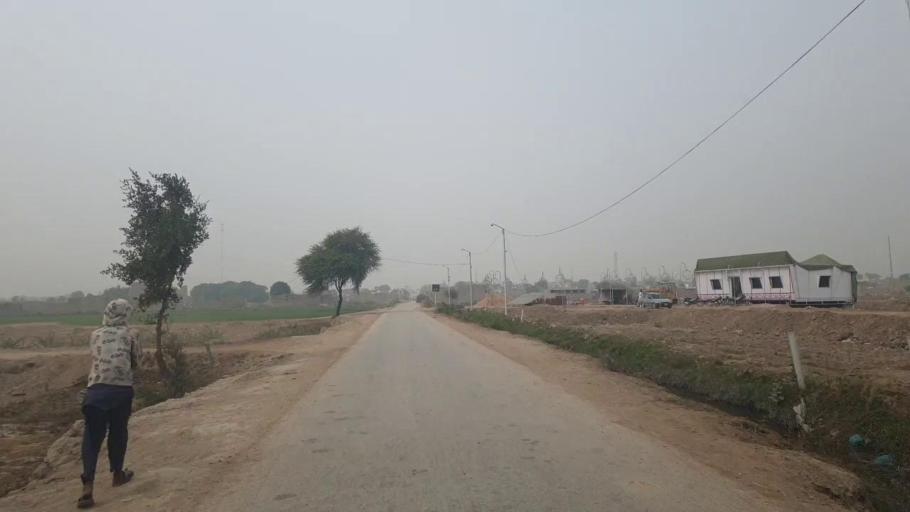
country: PK
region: Sindh
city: Tando Adam
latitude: 25.7508
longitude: 68.6699
